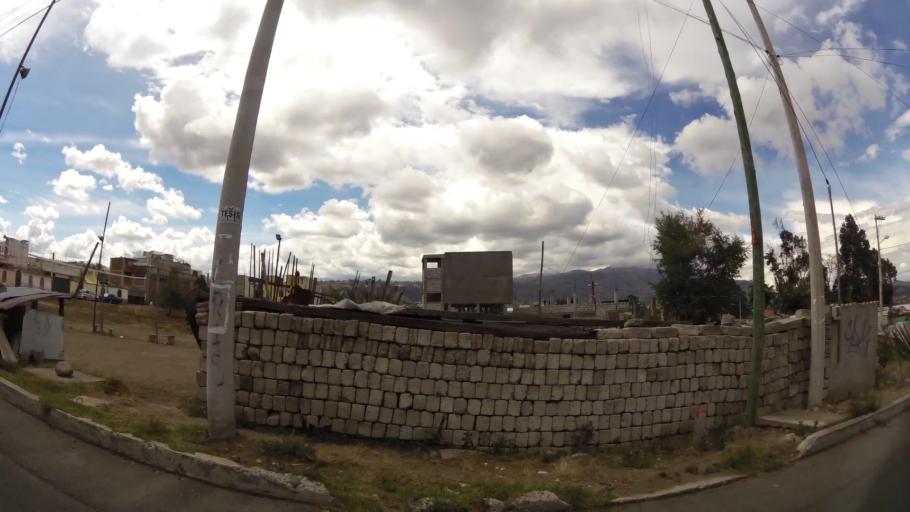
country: EC
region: Tungurahua
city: Ambato
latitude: -1.2611
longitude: -78.6112
